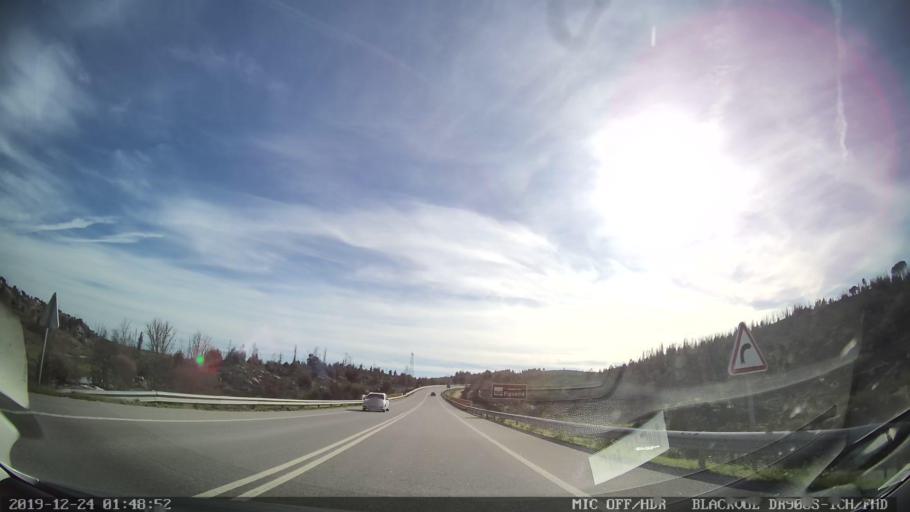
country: PT
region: Portalegre
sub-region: Nisa
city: Nisa
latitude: 39.5176
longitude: -7.7704
